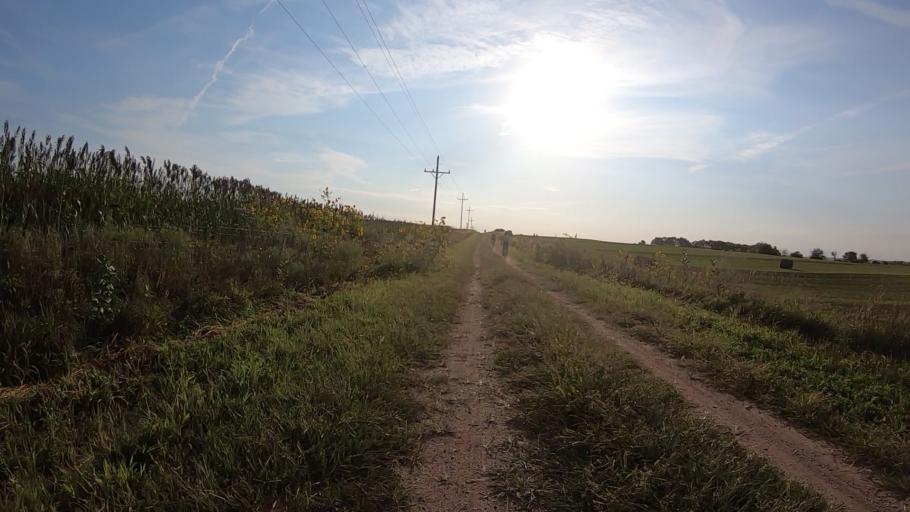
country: US
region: Kansas
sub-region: Marshall County
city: Blue Rapids
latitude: 39.7114
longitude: -96.8031
